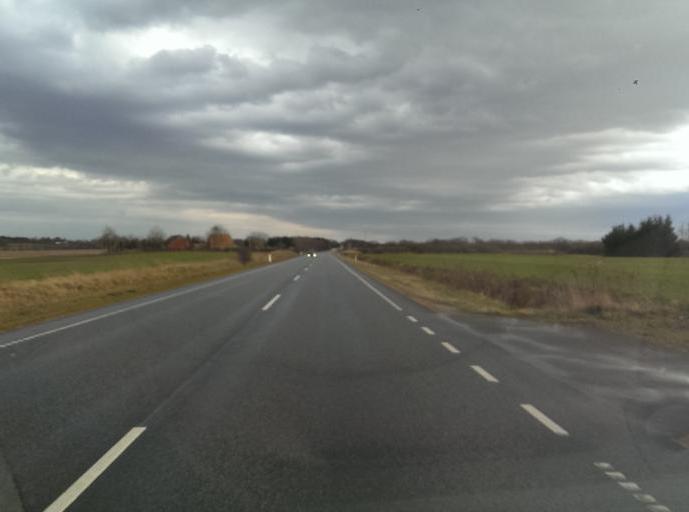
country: DK
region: South Denmark
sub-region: Esbjerg Kommune
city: Tjaereborg
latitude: 55.5022
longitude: 8.6081
